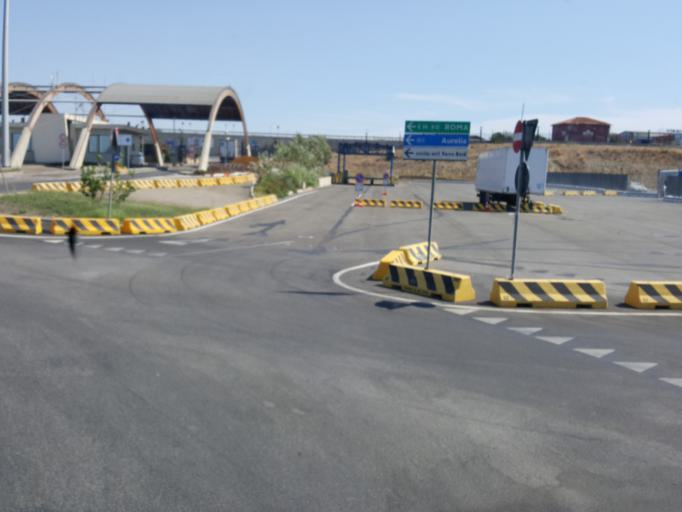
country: IT
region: Latium
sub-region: Citta metropolitana di Roma Capitale
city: Aurelia
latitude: 42.1154
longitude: 11.7696
